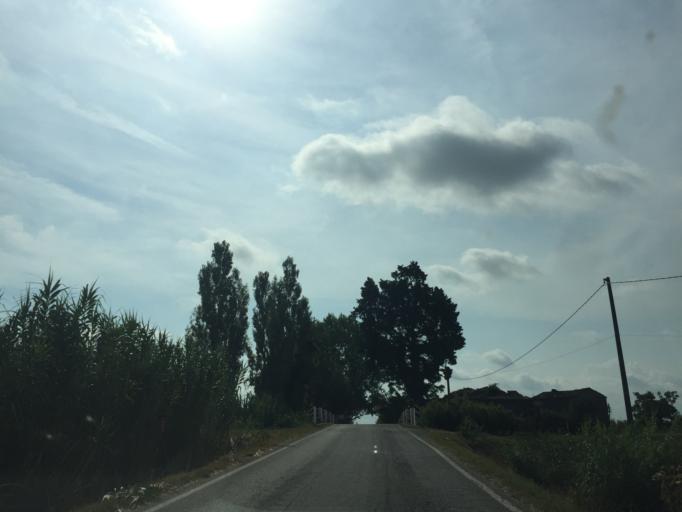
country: IT
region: Tuscany
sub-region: Provincia di Pistoia
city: Cintolese
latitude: 43.8473
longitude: 10.8110
